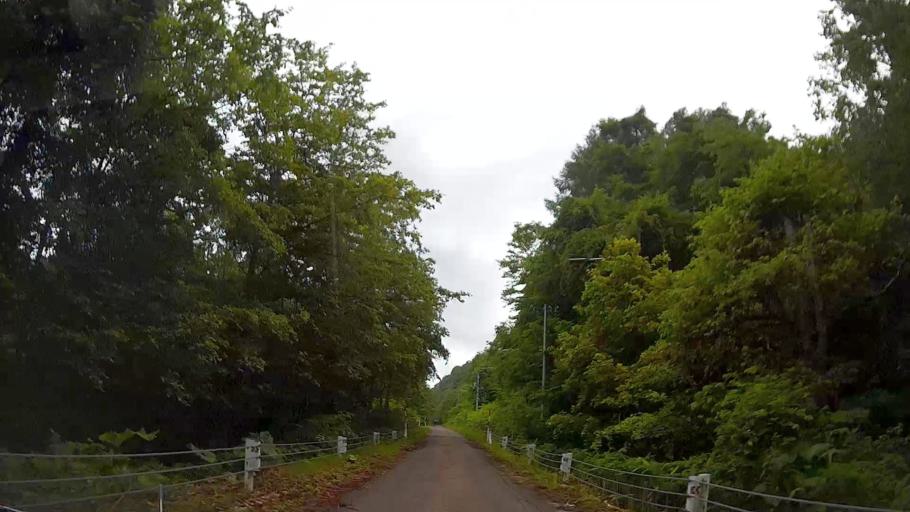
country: JP
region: Hokkaido
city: Nanae
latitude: 42.0650
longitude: 140.5018
